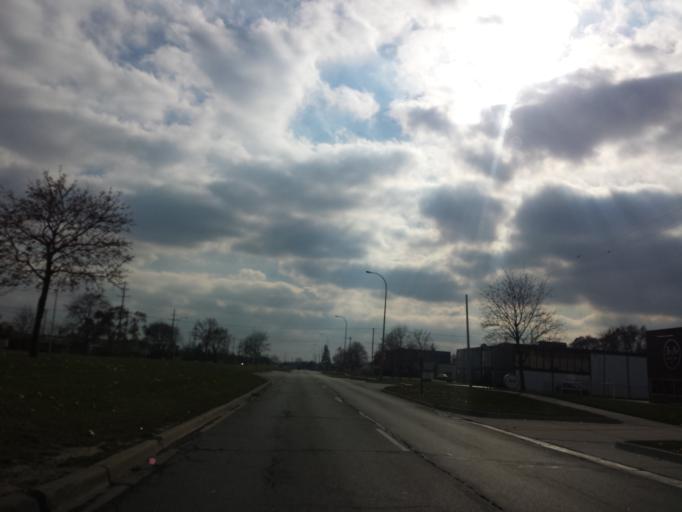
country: US
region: Michigan
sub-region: Oakland County
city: Clawson
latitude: 42.5247
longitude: -83.1199
